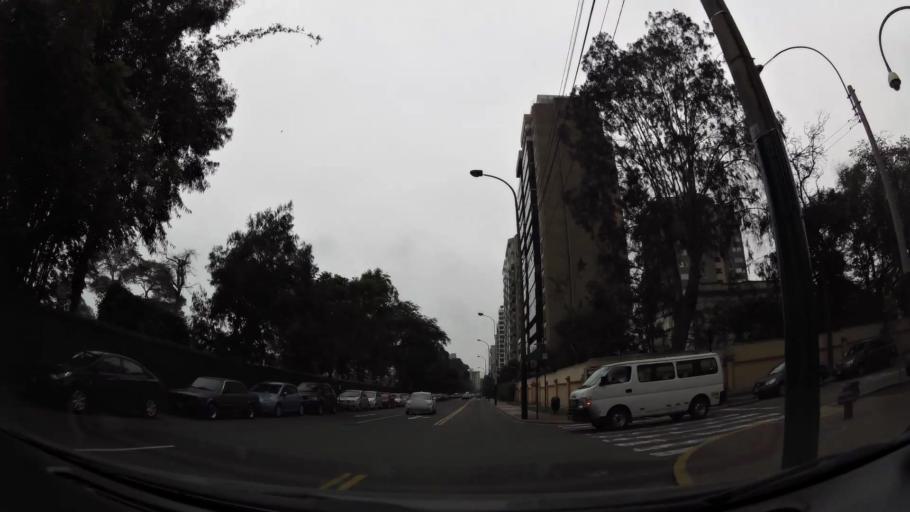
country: PE
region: Lima
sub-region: Lima
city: San Isidro
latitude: -12.0995
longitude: -77.0436
